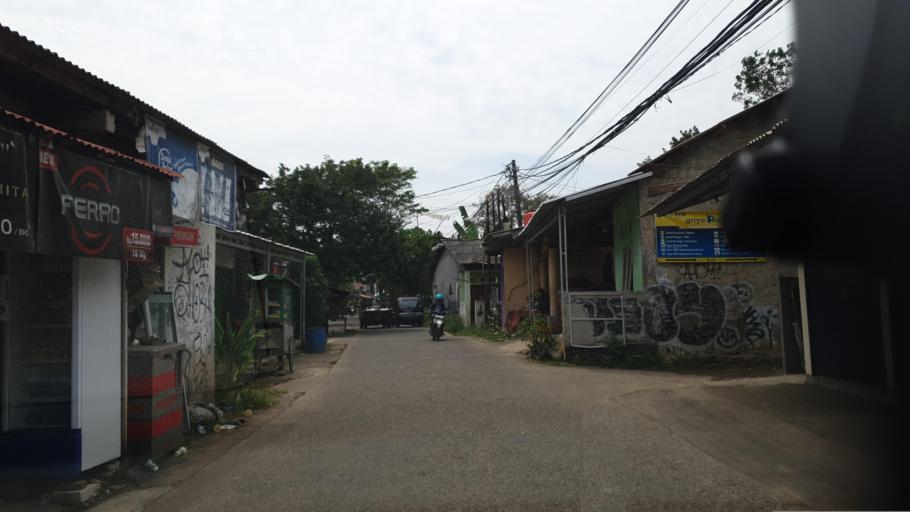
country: ID
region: West Java
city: Sawangan
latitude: -6.3786
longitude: 106.7603
